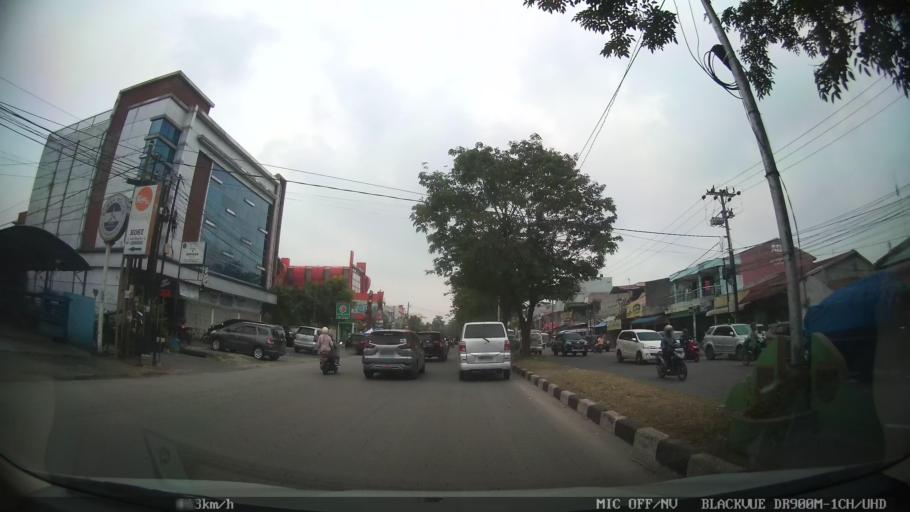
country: ID
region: North Sumatra
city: Deli Tua
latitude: 3.5467
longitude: 98.6987
